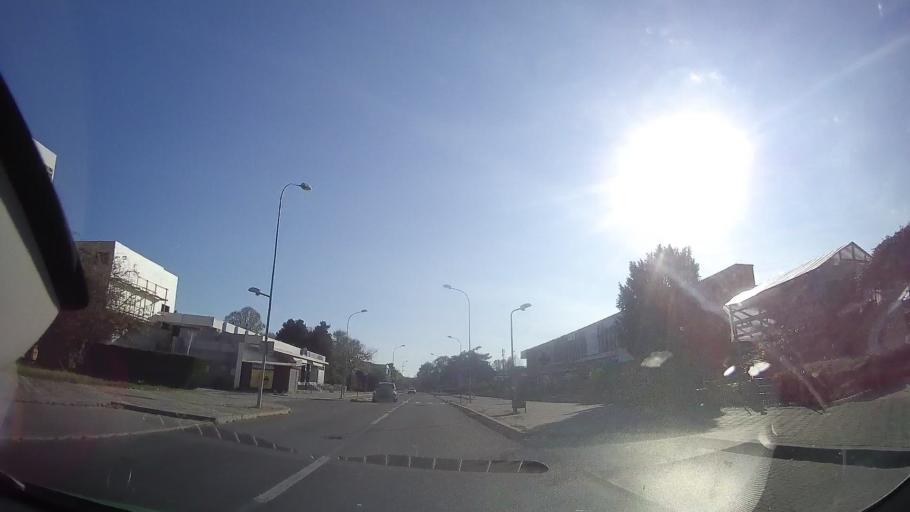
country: RO
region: Constanta
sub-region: Comuna Douazeci si Trei August
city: Douazeci si Trei August
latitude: 43.8674
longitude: 28.5974
